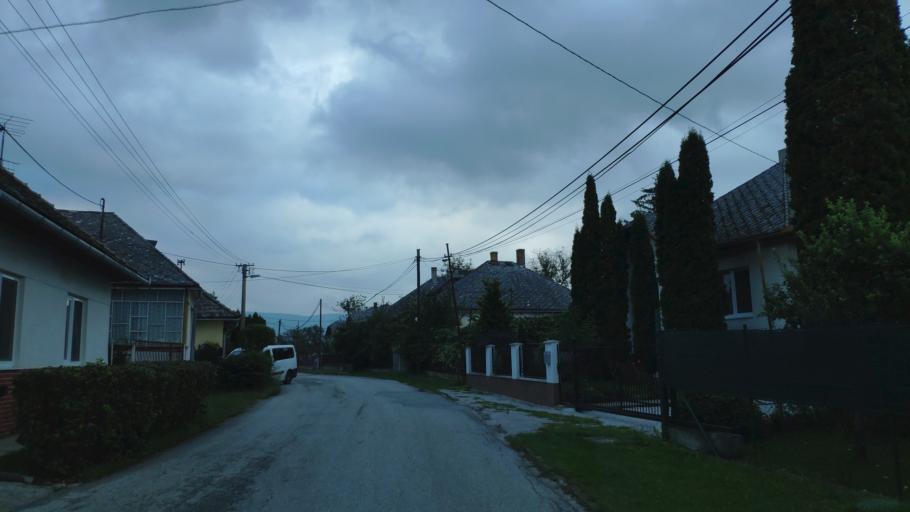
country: SK
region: Kosicky
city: Moldava nad Bodvou
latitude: 48.5811
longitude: 20.8877
